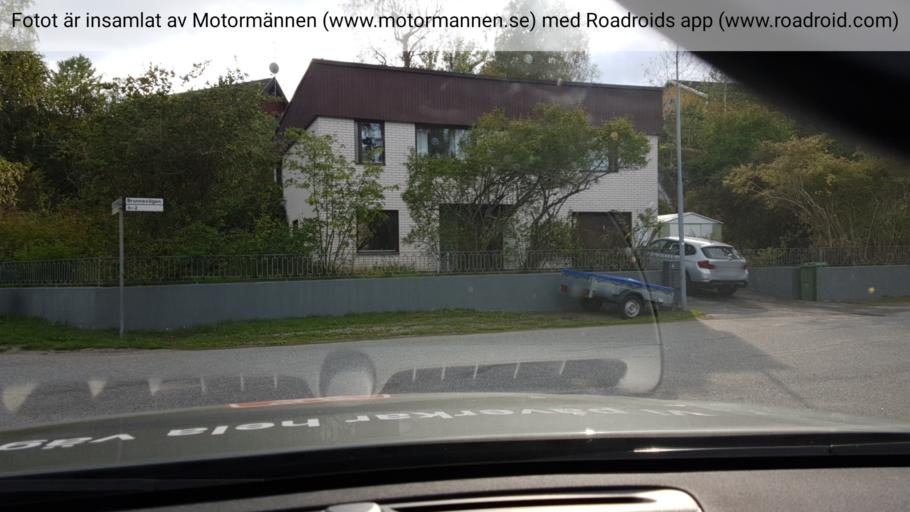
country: SE
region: Stockholm
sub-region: Huddinge Kommun
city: Huddinge
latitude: 59.2290
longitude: 17.9795
